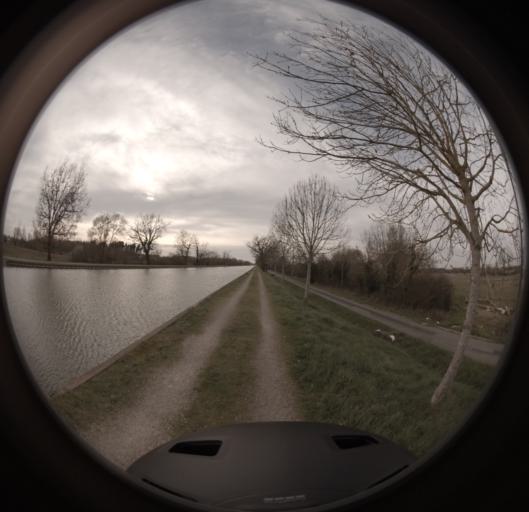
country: FR
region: Midi-Pyrenees
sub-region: Departement du Tarn-et-Garonne
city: Montbeton
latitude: 43.9839
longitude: 1.2768
